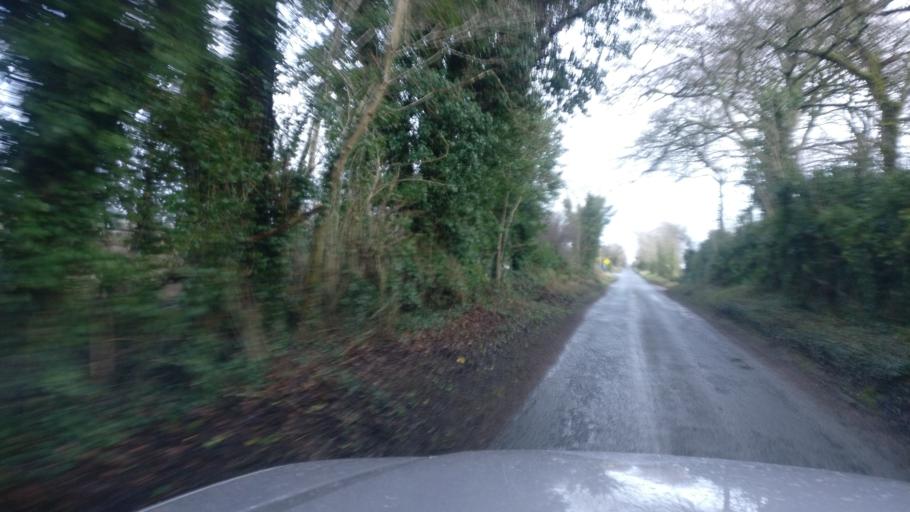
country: IE
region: Connaught
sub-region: County Galway
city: Athenry
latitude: 53.2631
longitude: -8.7010
